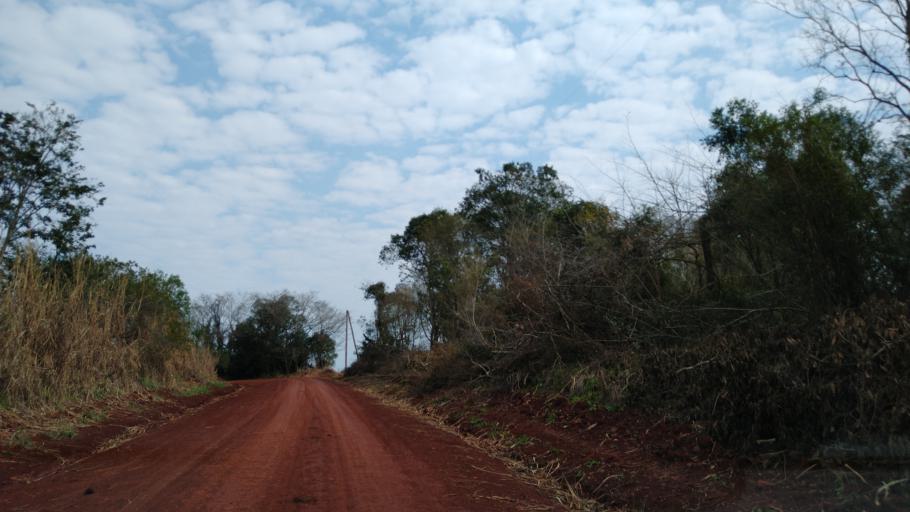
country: AR
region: Misiones
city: Capiovi
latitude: -26.9423
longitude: -55.0668
